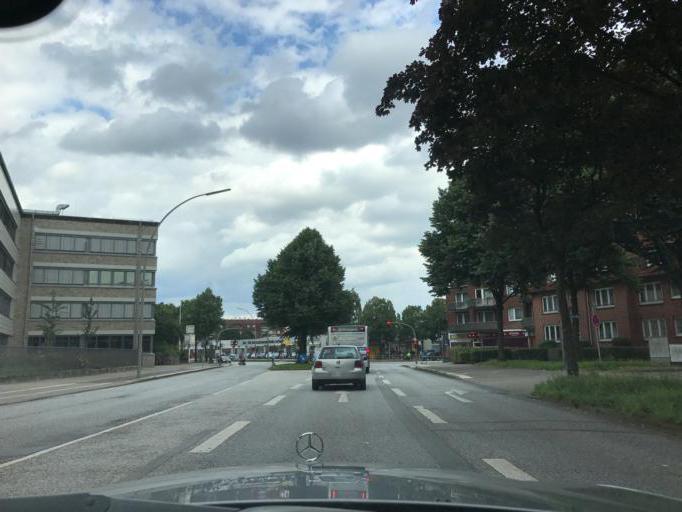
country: DE
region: Hamburg
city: Wandsbek
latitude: 53.5379
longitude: 10.1092
